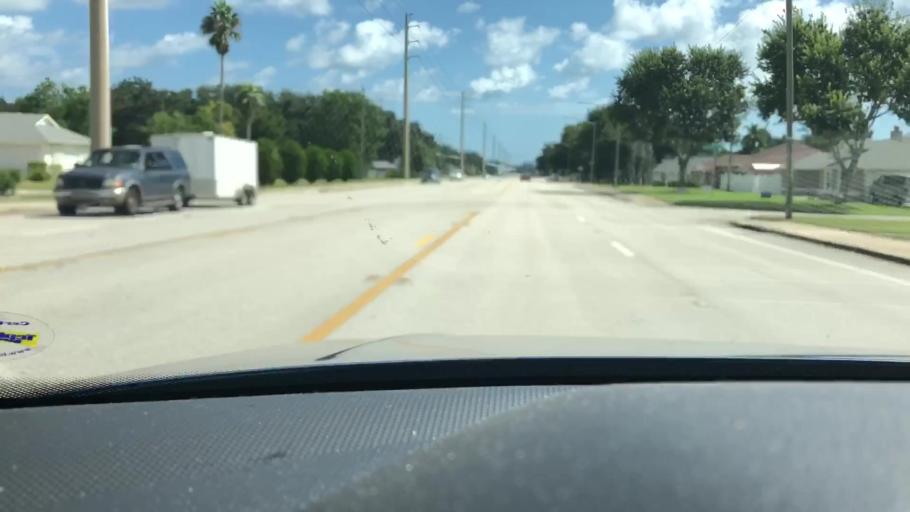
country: US
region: Florida
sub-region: Volusia County
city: Edgewater
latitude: 28.9658
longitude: -80.9135
